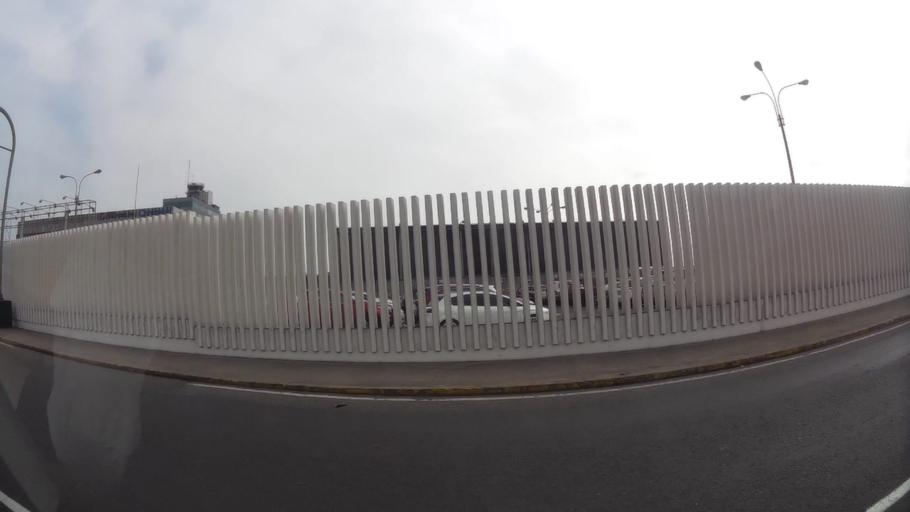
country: PE
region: Callao
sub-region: Callao
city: Callao
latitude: -12.0222
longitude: -77.1073
